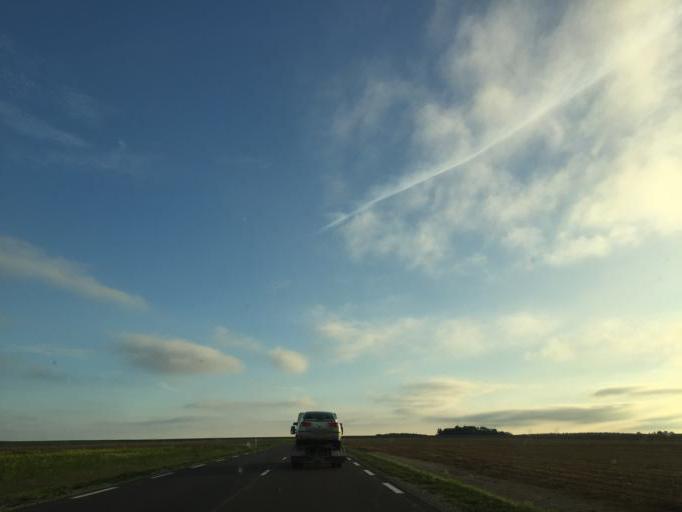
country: FR
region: Bourgogne
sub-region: Departement de l'Yonne
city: Sergines
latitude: 48.3611
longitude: 3.2327
